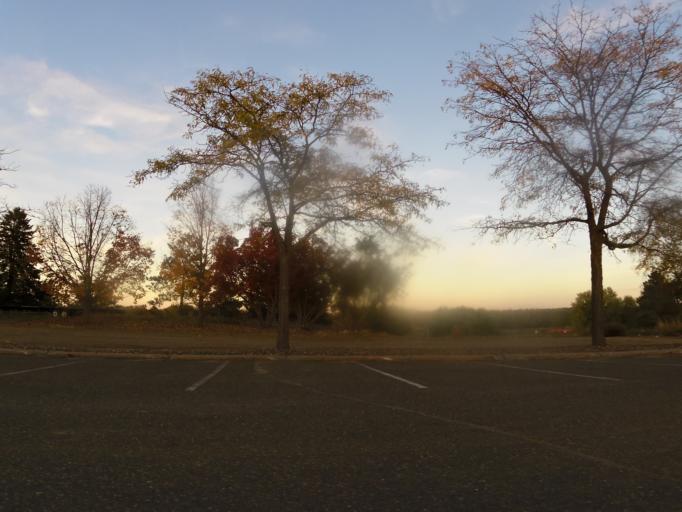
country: US
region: Minnesota
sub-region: Washington County
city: Lake Elmo
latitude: 44.9749
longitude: -92.8692
